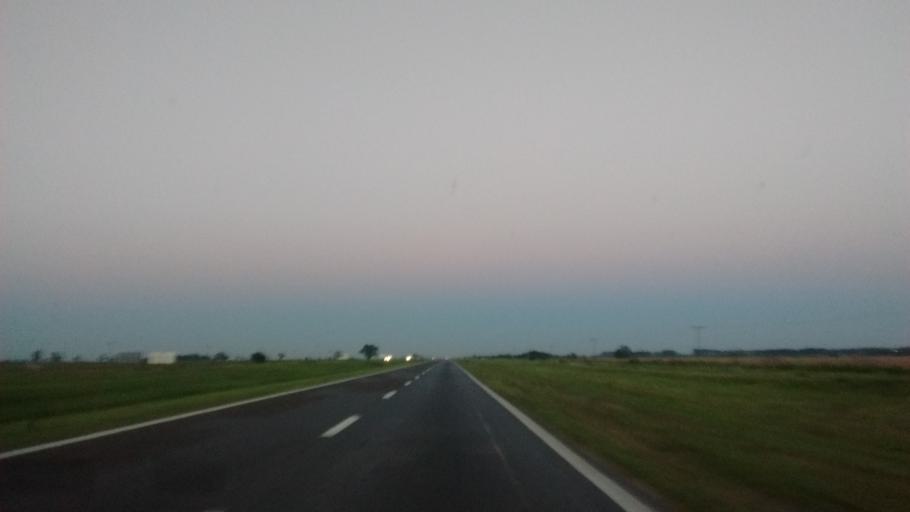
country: AR
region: Santa Fe
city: Roldan
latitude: -32.9163
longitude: -60.9452
